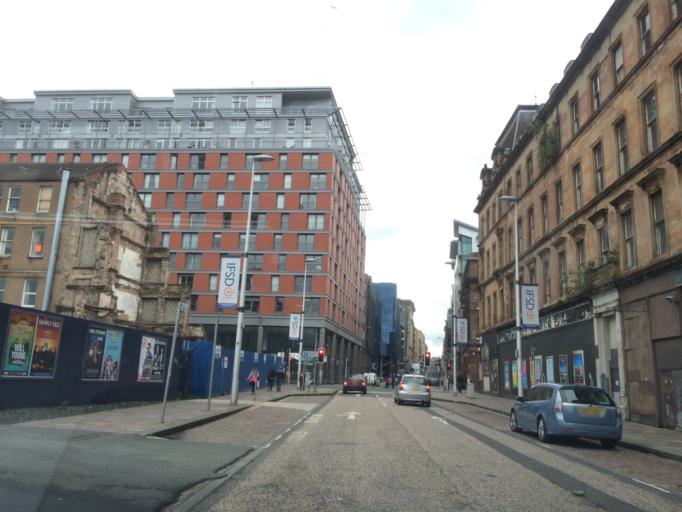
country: GB
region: Scotland
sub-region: Glasgow City
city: Glasgow
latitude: 55.8582
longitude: -4.2626
